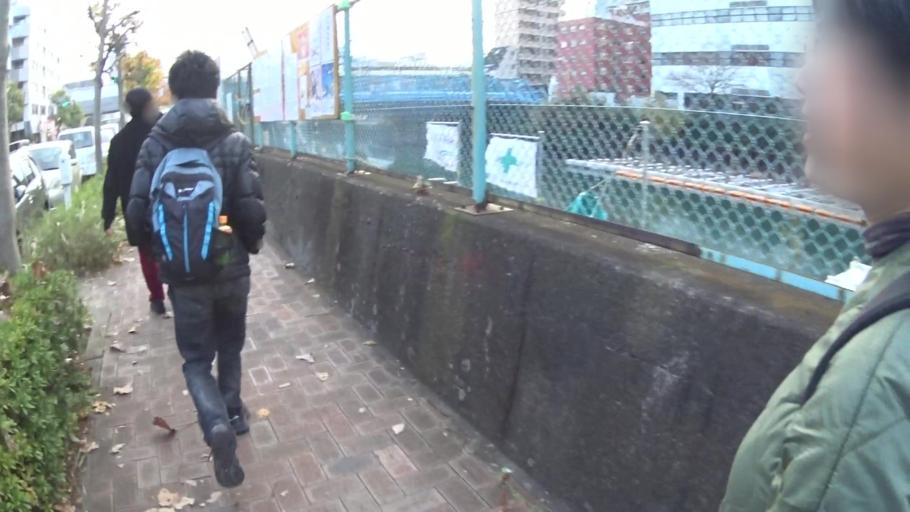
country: JP
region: Tokyo
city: Urayasu
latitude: 35.6948
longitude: 139.8196
